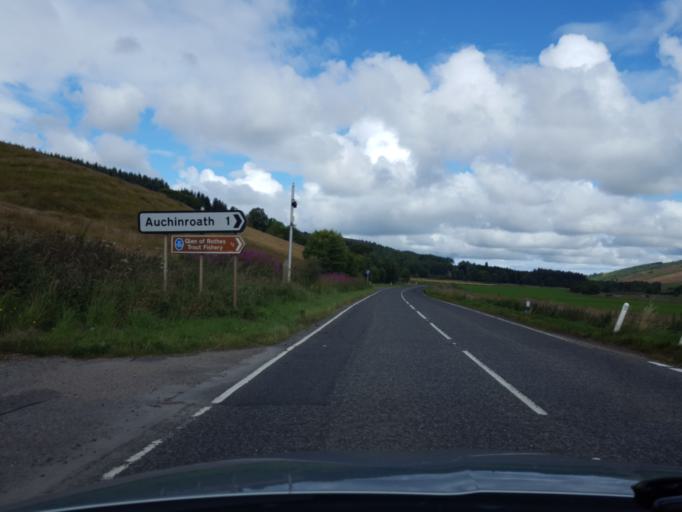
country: GB
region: Scotland
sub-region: Moray
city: Rothes
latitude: 57.5472
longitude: -3.2357
